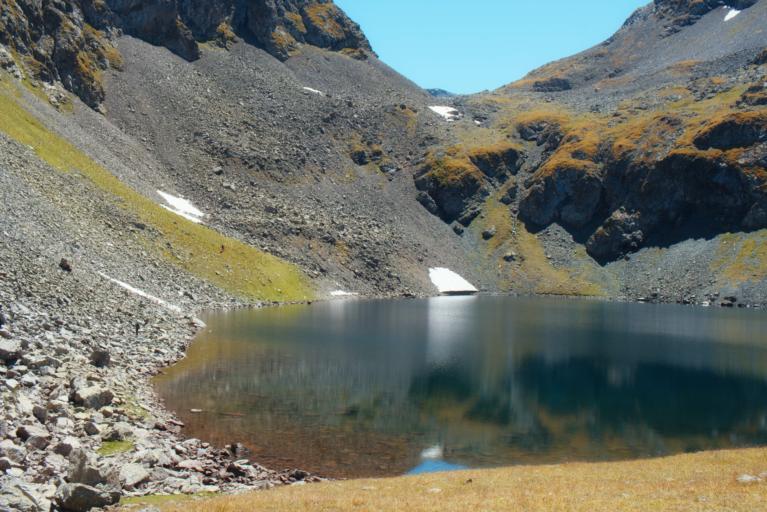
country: RU
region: Karachayevo-Cherkesiya
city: Nizhniy Arkhyz
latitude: 43.6022
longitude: 41.1684
